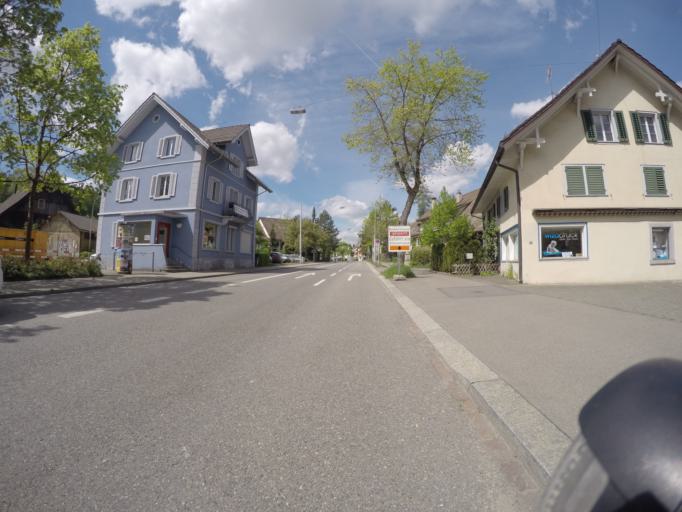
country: CH
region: Zurich
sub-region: Bezirk Zuerich
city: Zuerich (Kreis 12) / Schwamendingen-Mitte
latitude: 47.4037
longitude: 8.5711
